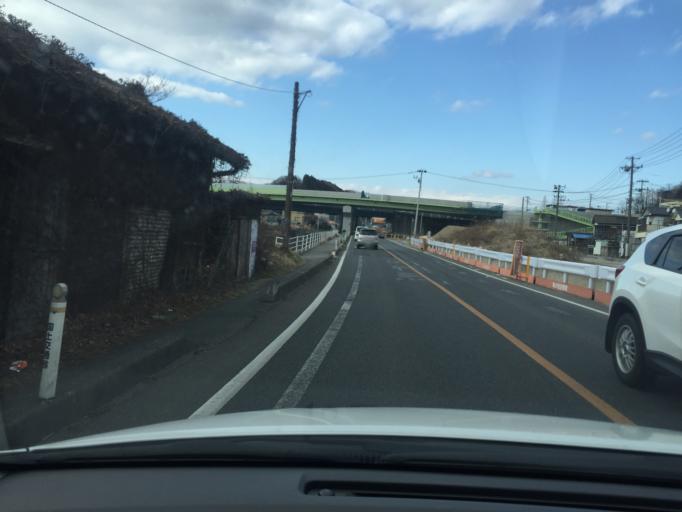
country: JP
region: Fukushima
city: Iwaki
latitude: 37.0084
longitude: 140.8499
